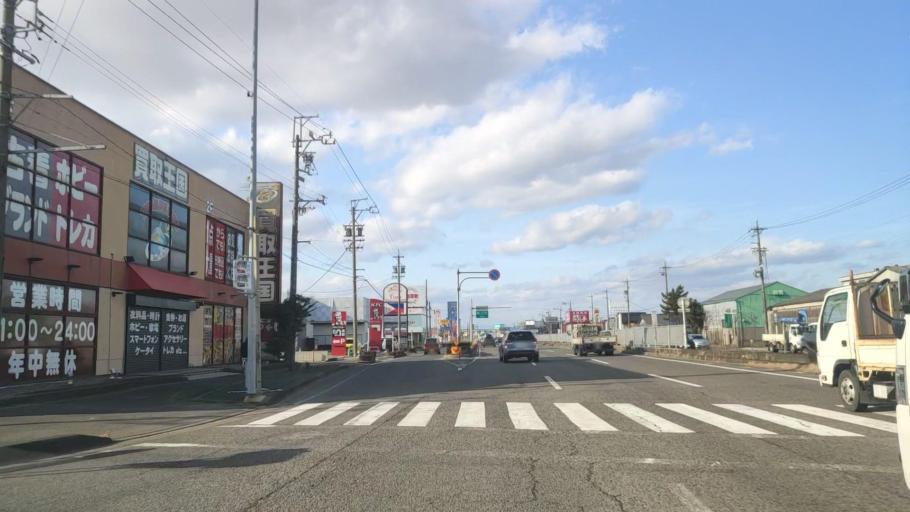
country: JP
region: Aichi
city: Ichinomiya
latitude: 35.3063
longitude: 136.8203
